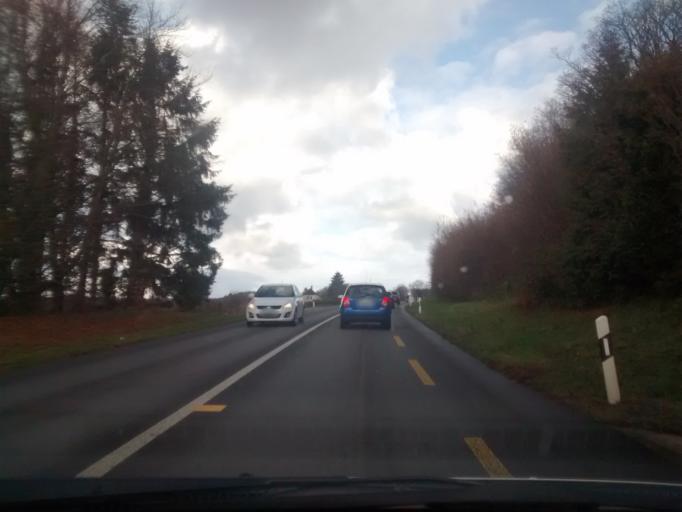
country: CH
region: Vaud
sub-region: Ouest Lausannois District
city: Crissier
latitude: 46.5659
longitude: 6.5786
